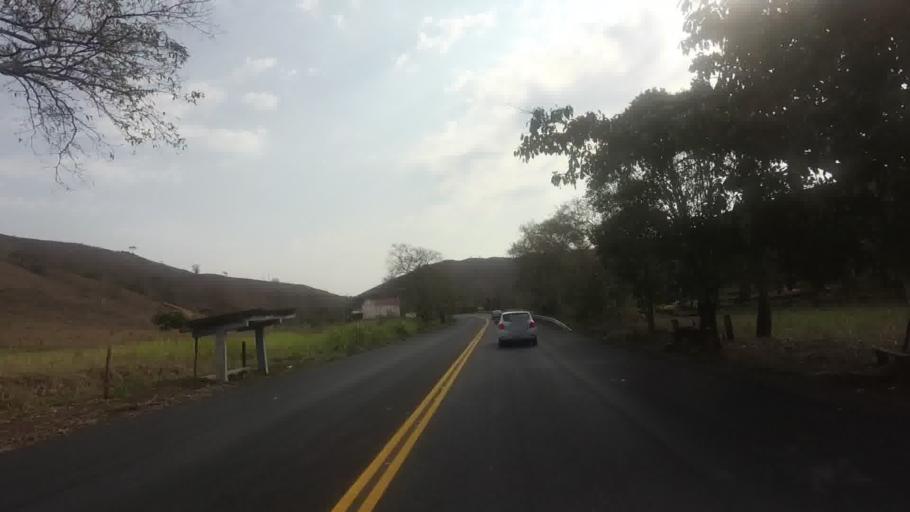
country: BR
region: Rio de Janeiro
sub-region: Bom Jesus Do Itabapoana
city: Bom Jesus do Itabapoana
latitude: -21.2123
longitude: -41.7320
